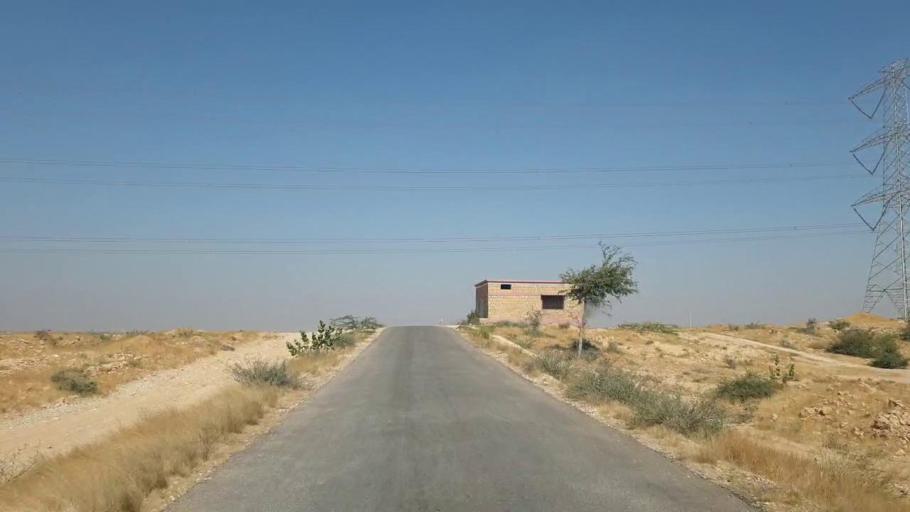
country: PK
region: Sindh
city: Thatta
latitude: 25.2025
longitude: 67.7976
